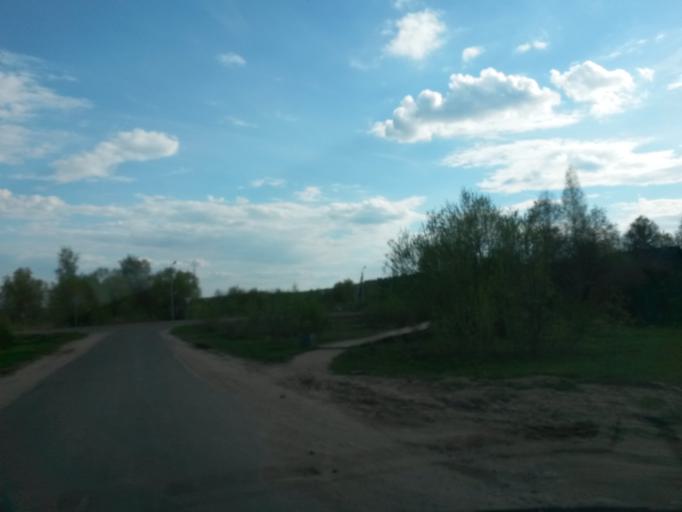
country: RU
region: Jaroslavl
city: Myshkin
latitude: 57.7815
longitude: 38.4485
